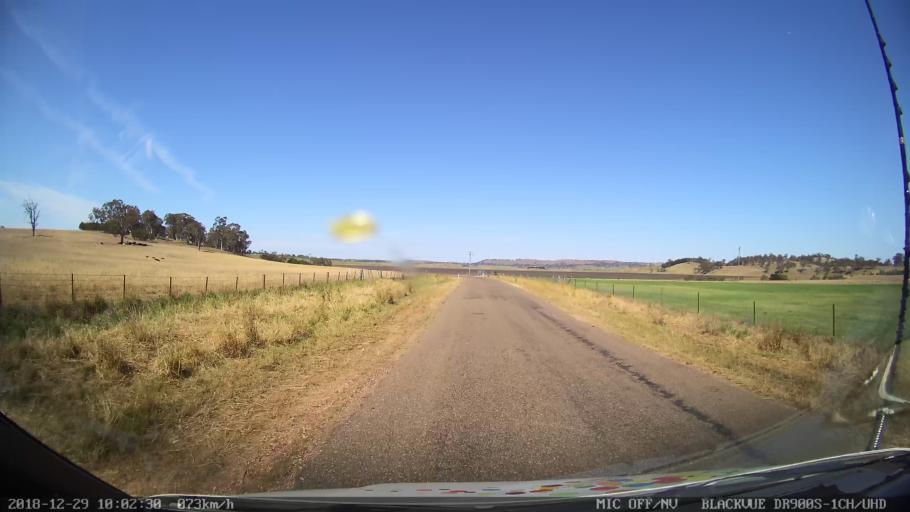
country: AU
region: New South Wales
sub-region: Goulburn Mulwaree
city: Goulburn
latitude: -34.8018
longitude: 149.4635
